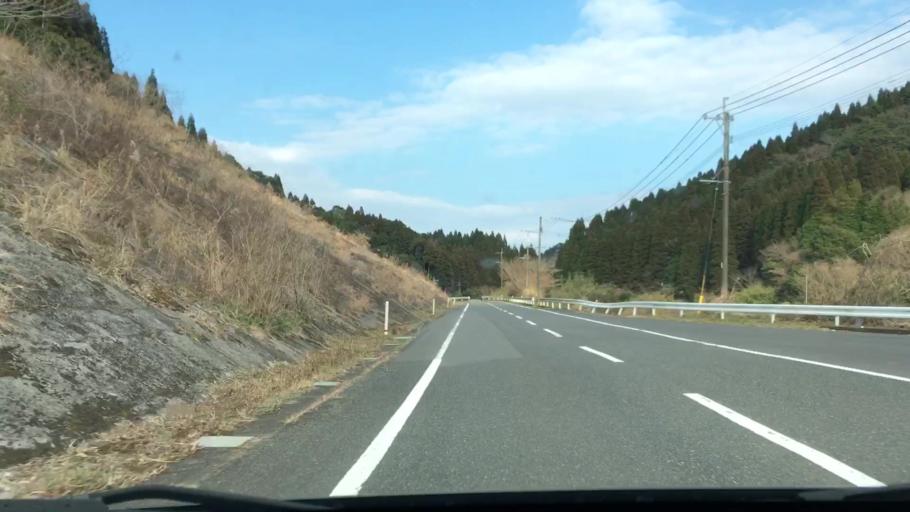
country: JP
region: Miyazaki
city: Kushima
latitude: 31.5685
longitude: 131.2604
